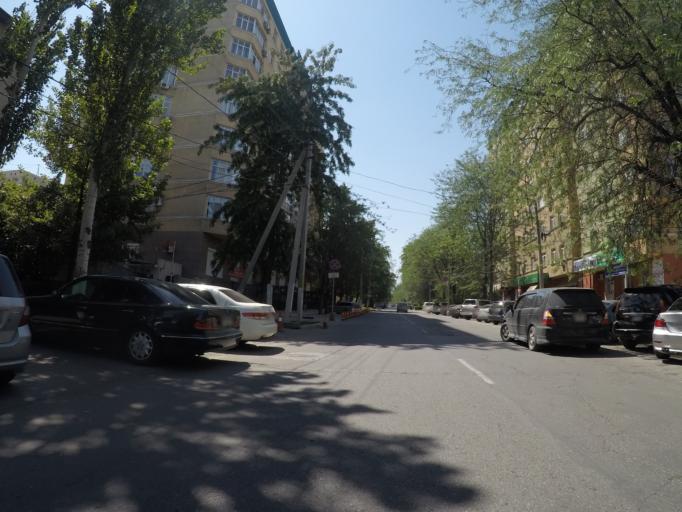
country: KG
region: Chuy
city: Bishkek
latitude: 42.8811
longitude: 74.5922
